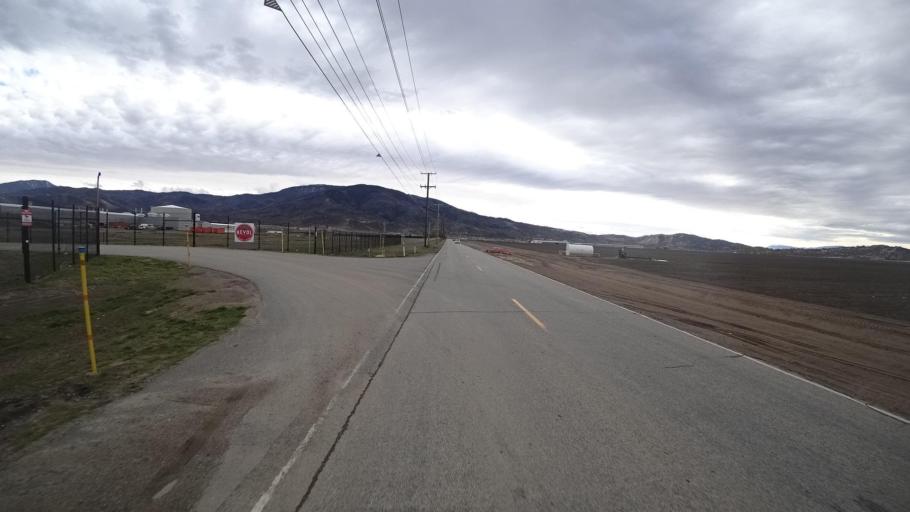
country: US
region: California
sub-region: Kern County
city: Stallion Springs
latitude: 35.1164
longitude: -118.6018
